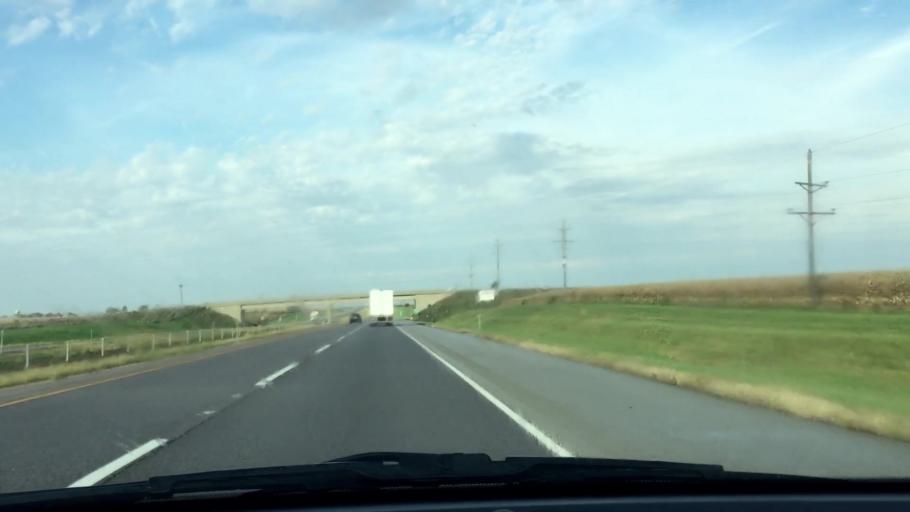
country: US
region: Illinois
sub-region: Lee County
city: Franklin Grove
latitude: 41.8229
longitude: -89.3585
